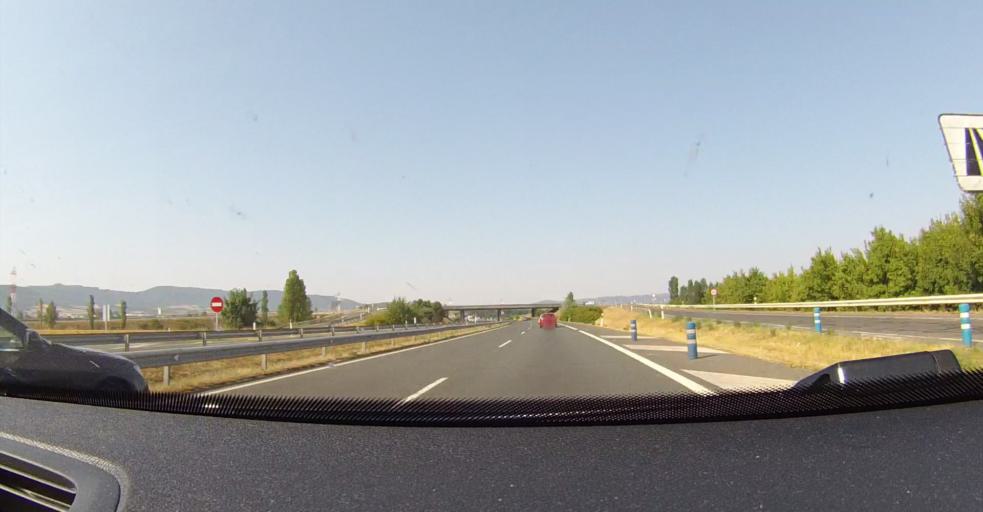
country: ES
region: Basque Country
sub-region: Provincia de Alava
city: Gasteiz / Vitoria
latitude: 42.8632
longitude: -2.7370
